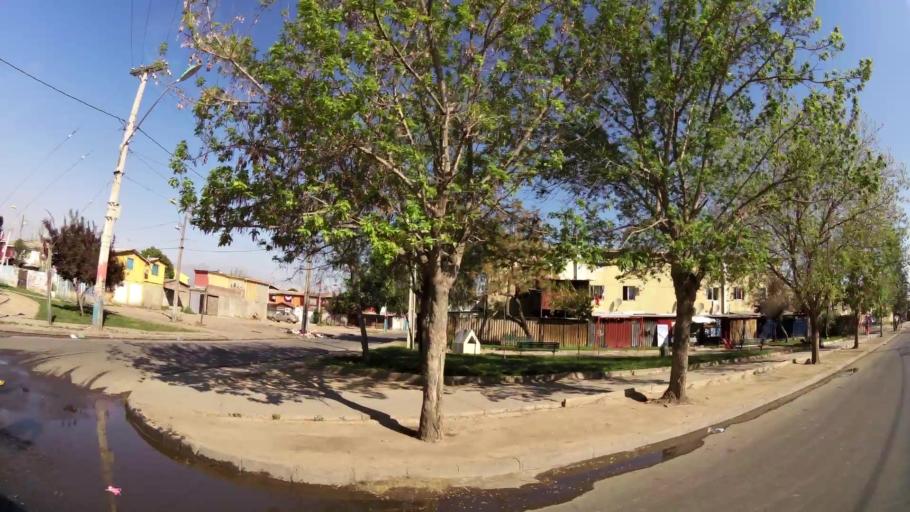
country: CL
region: Santiago Metropolitan
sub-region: Provincia de Santiago
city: La Pintana
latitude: -33.5610
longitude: -70.6159
